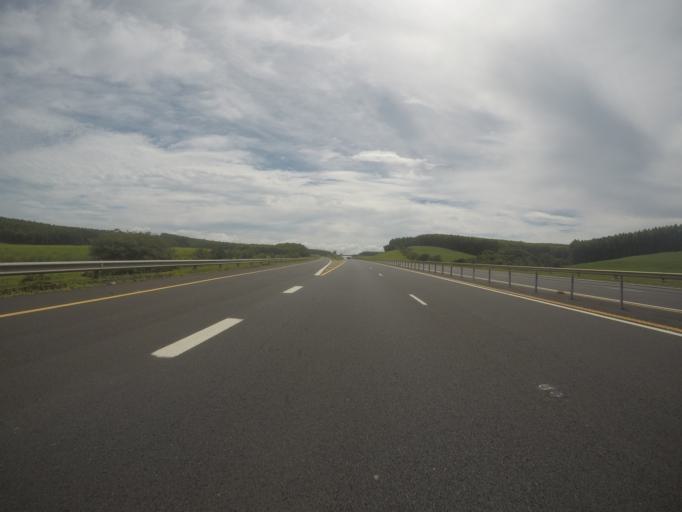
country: ZA
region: KwaZulu-Natal
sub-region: uThungulu District Municipality
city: Eshowe
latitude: -29.0459
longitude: 31.6435
